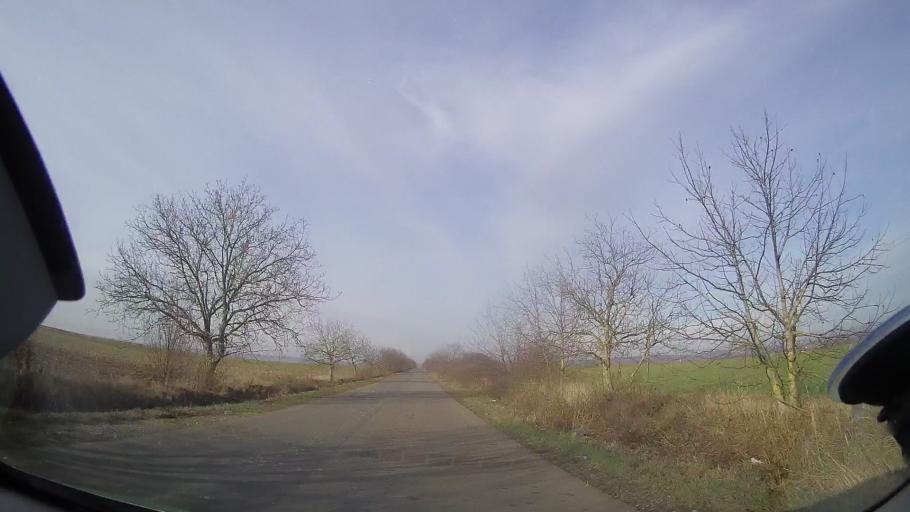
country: RO
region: Bihor
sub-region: Comuna Spinus
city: Spinus
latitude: 47.2166
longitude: 22.1749
